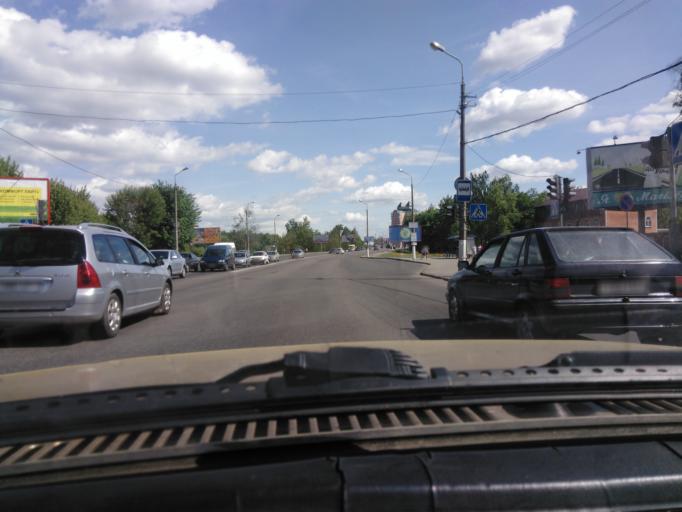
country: BY
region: Mogilev
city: Mahilyow
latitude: 53.9167
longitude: 30.3130
